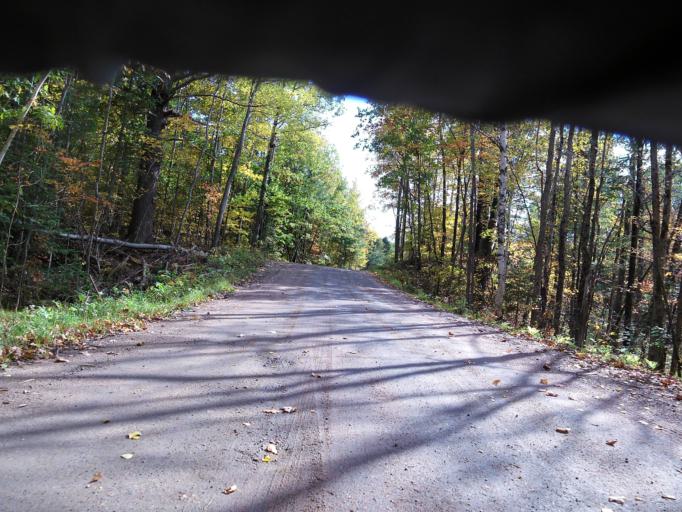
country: CA
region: Ontario
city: Petawawa
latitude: 45.8074
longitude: -77.3234
